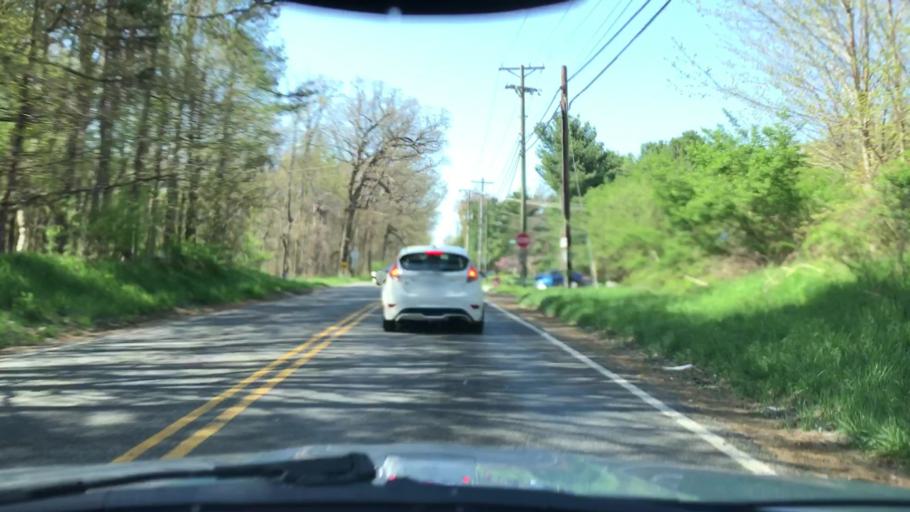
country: US
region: Indiana
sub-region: Saint Joseph County
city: Georgetown
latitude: 41.7441
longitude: -86.2974
